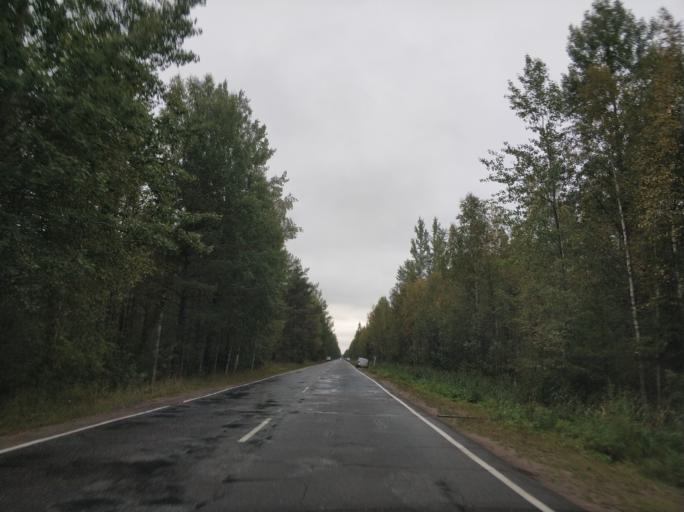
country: RU
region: Leningrad
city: Borisova Griva
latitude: 60.1652
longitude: 30.9209
